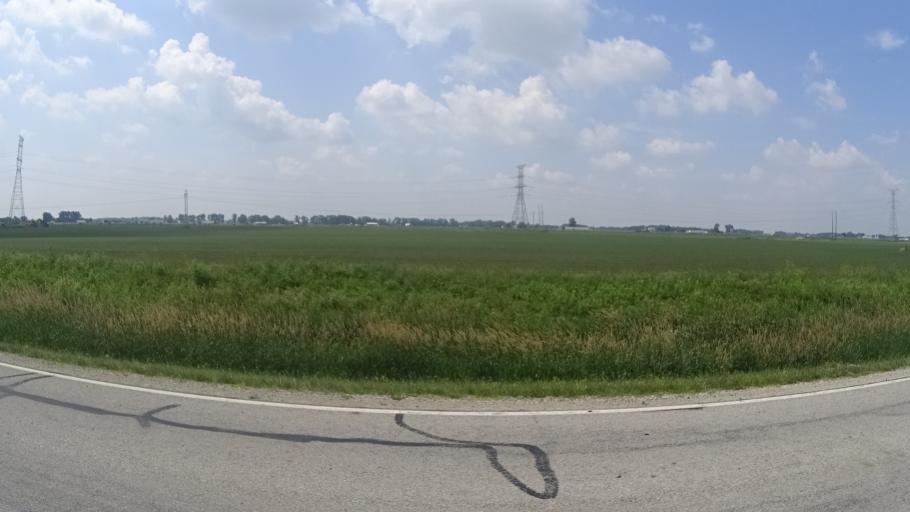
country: US
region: Ohio
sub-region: Erie County
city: Milan
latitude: 41.3352
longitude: -82.6493
